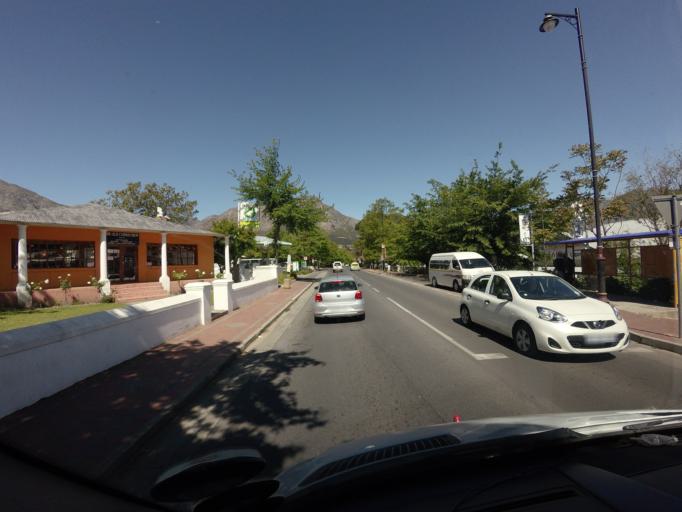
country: ZA
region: Western Cape
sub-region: Cape Winelands District Municipality
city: Paarl
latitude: -33.9049
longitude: 19.1123
